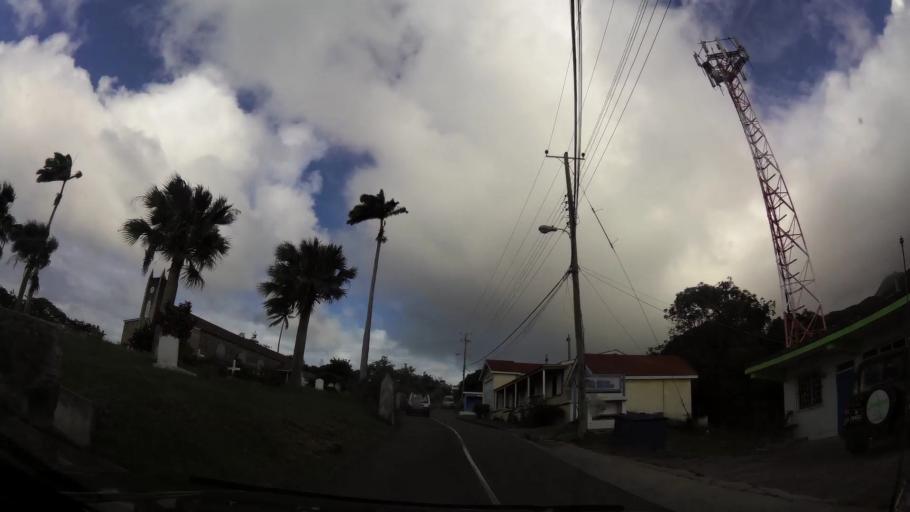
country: MS
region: Saint Peter
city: Saint Peters
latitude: 16.7740
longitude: -62.2159
